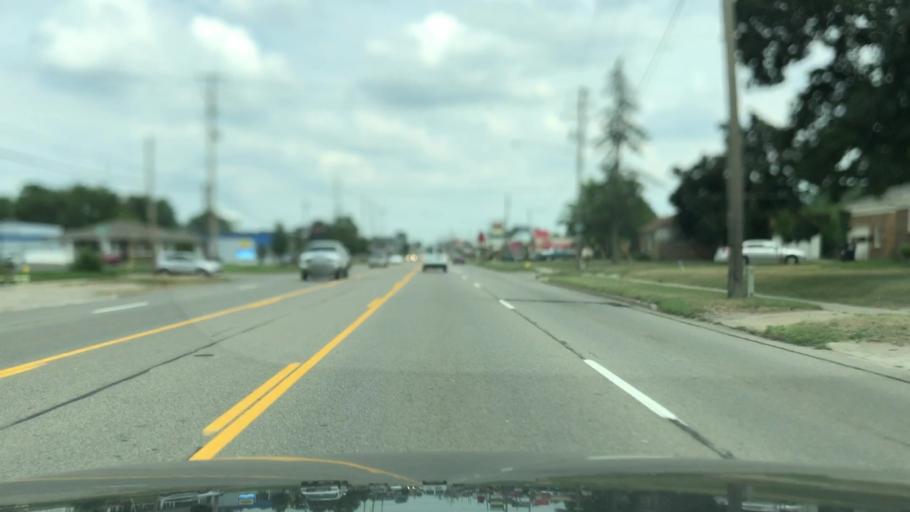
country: US
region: Michigan
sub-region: Kent County
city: Wyoming
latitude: 42.9137
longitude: -85.7137
